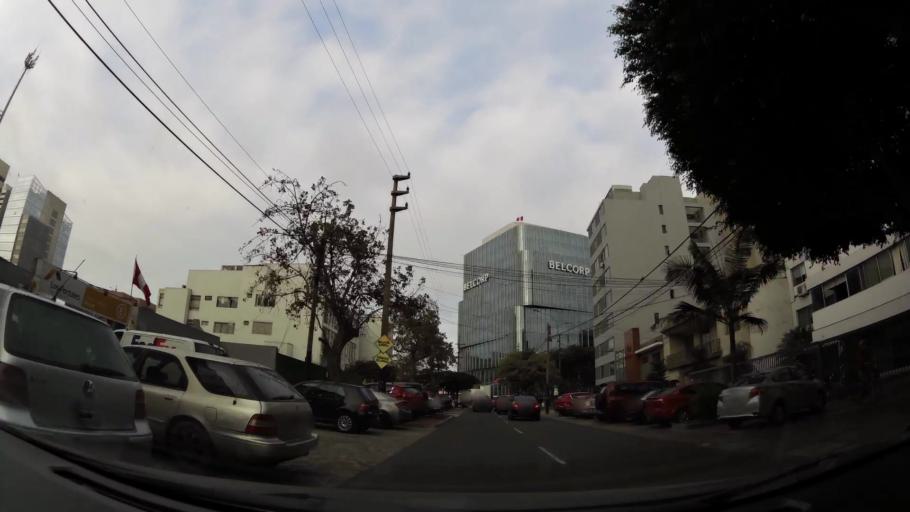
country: PE
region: Lima
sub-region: Lima
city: San Isidro
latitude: -12.1055
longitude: -77.0398
